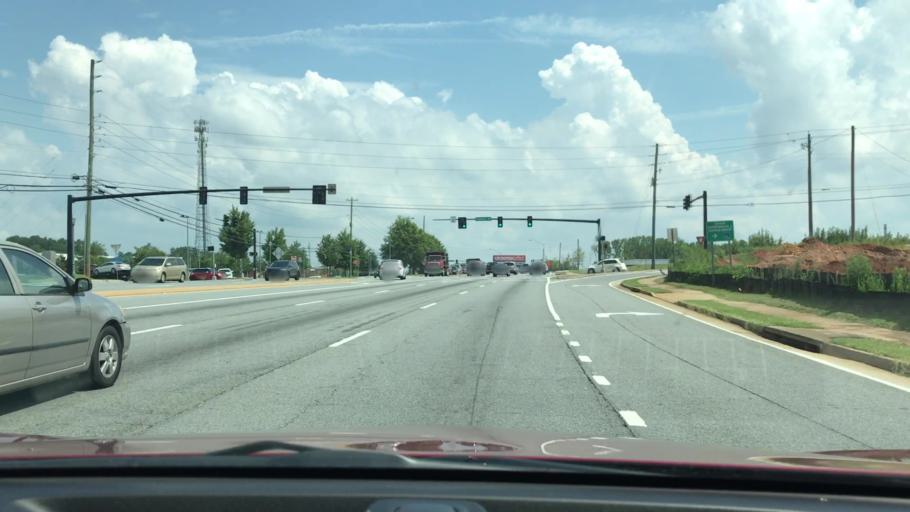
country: US
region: Georgia
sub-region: Gwinnett County
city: Buford
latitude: 34.0834
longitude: -83.9884
